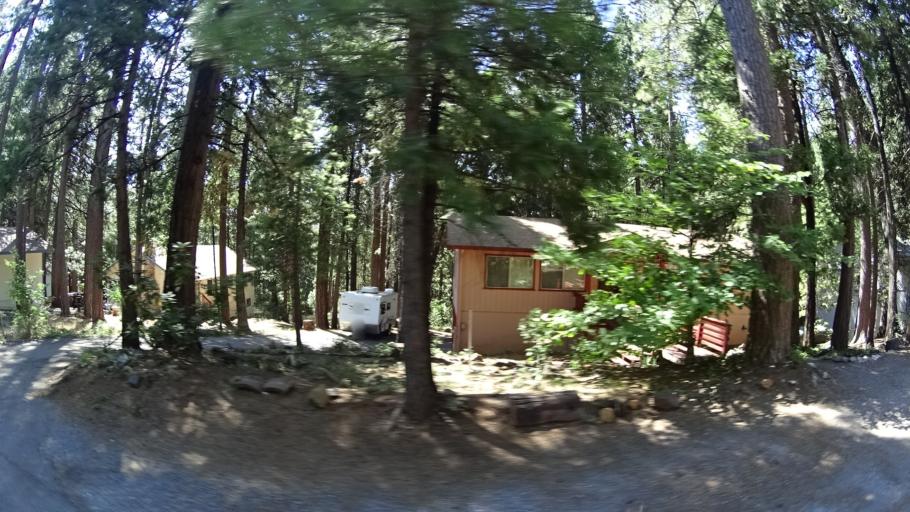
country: US
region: California
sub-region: Calaveras County
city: Arnold
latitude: 38.2504
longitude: -120.3671
